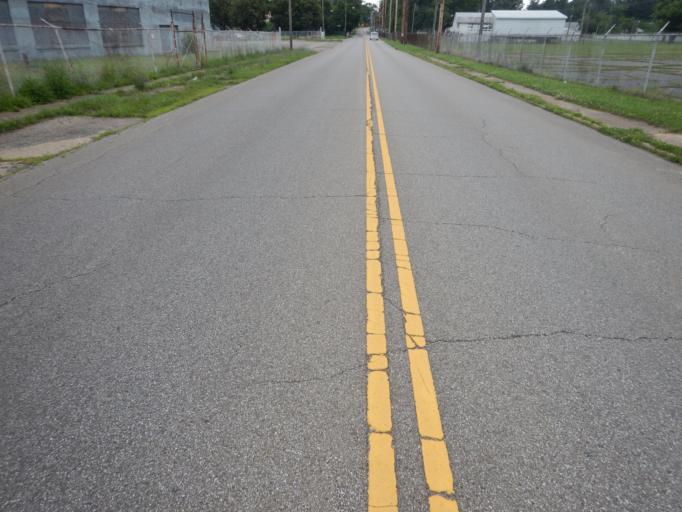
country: US
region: Ohio
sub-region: Muskingum County
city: Zanesville
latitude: 39.9242
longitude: -82.0259
